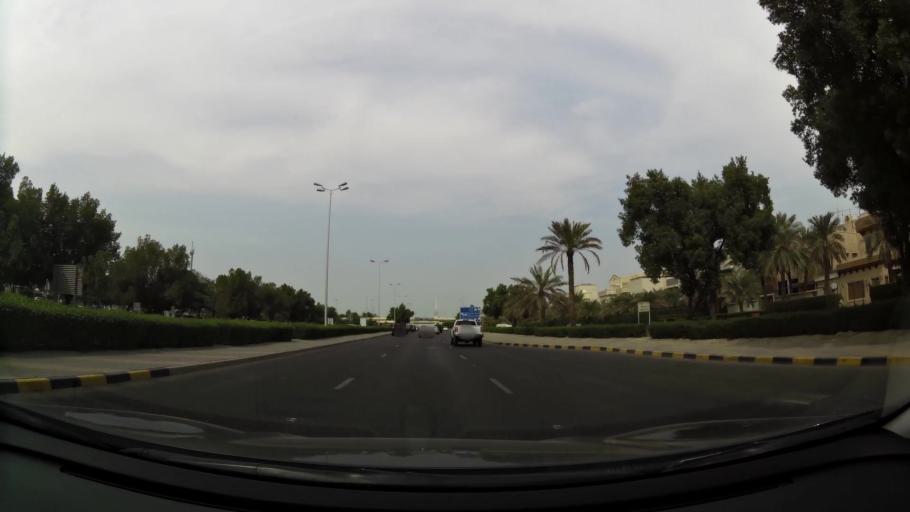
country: KW
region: Al Asimah
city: Ash Shamiyah
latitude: 29.3326
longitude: 47.9885
